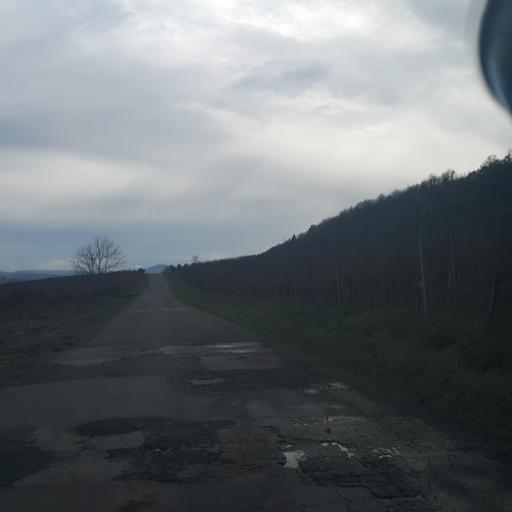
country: RS
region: Central Serbia
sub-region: Zajecarski Okrug
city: Knjazevac
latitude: 43.6179
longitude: 22.2610
